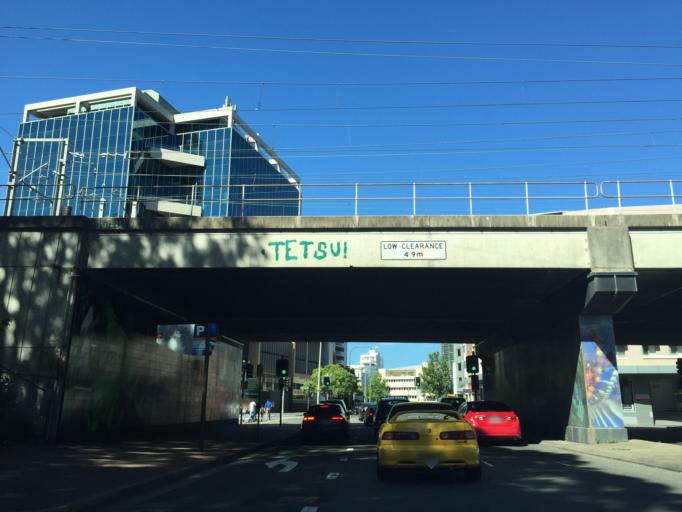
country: AU
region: New South Wales
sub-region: Parramatta
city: Harris Park
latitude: -33.8196
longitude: 151.0069
